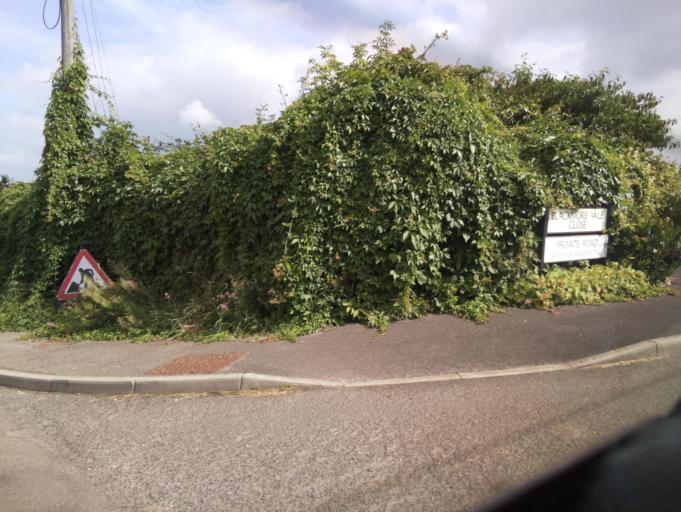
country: GB
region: England
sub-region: Somerset
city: Wincanton
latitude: 51.0047
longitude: -2.4191
